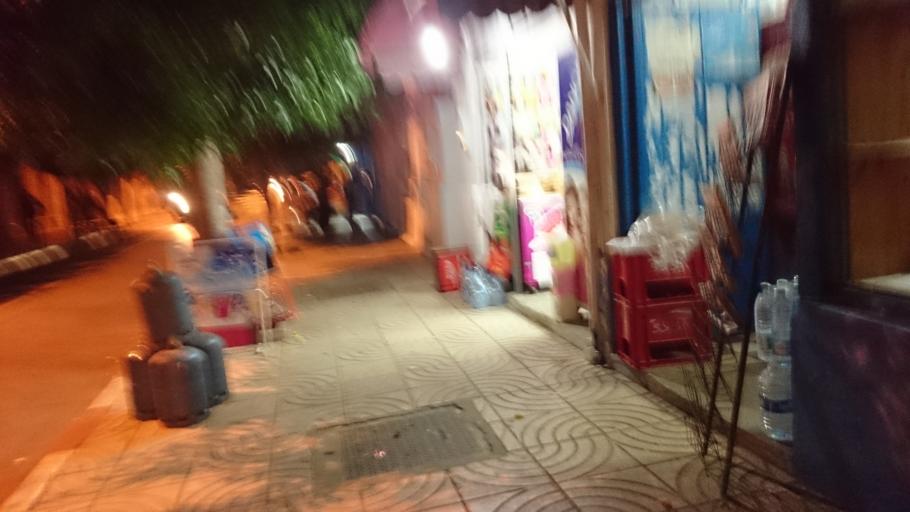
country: MA
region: Tanger-Tetouan
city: Asilah
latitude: 35.4676
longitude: -6.0320
